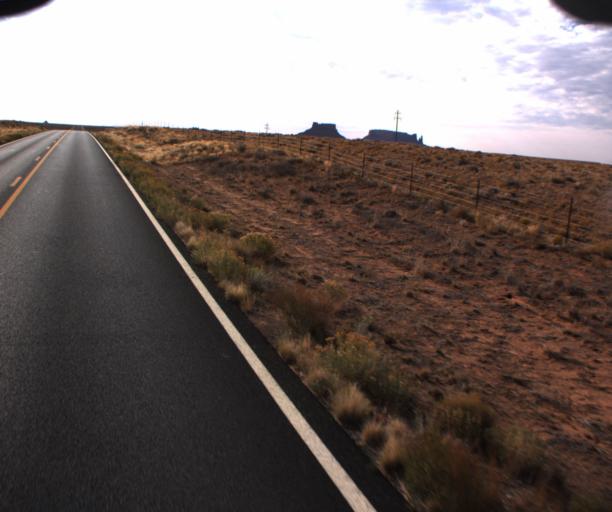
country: US
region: Arizona
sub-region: Apache County
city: Many Farms
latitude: 36.5849
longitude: -109.5579
